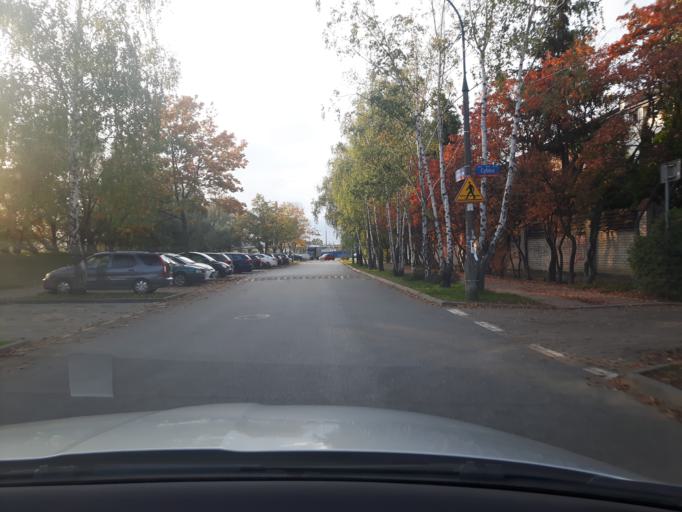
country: PL
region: Masovian Voivodeship
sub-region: Warszawa
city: Ursynow
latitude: 52.1524
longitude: 21.0221
